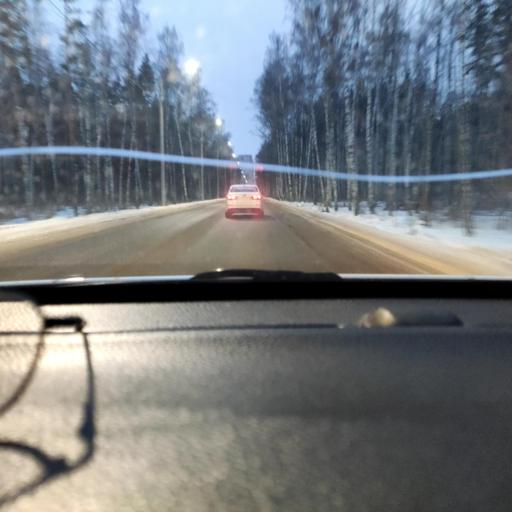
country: RU
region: Voronezj
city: Somovo
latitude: 51.6989
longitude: 39.2818
